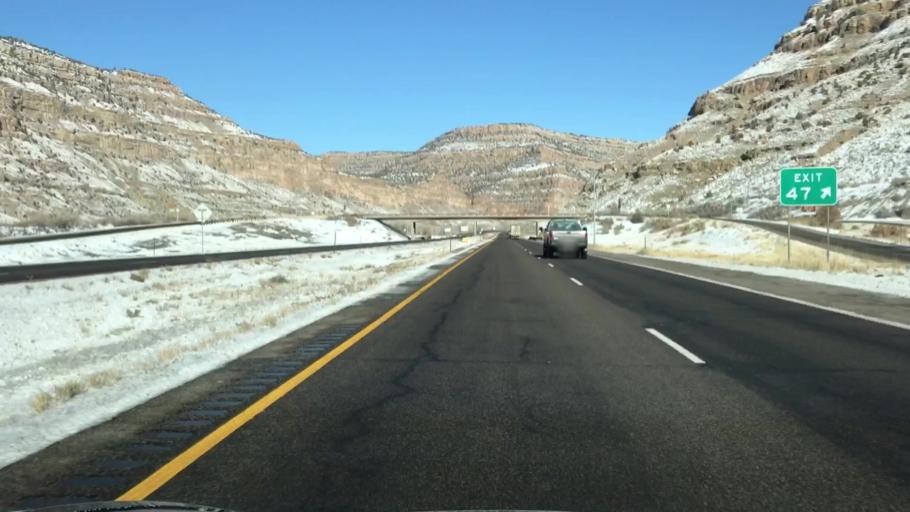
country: US
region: Colorado
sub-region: Mesa County
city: Palisade
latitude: 39.1583
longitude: -108.3009
